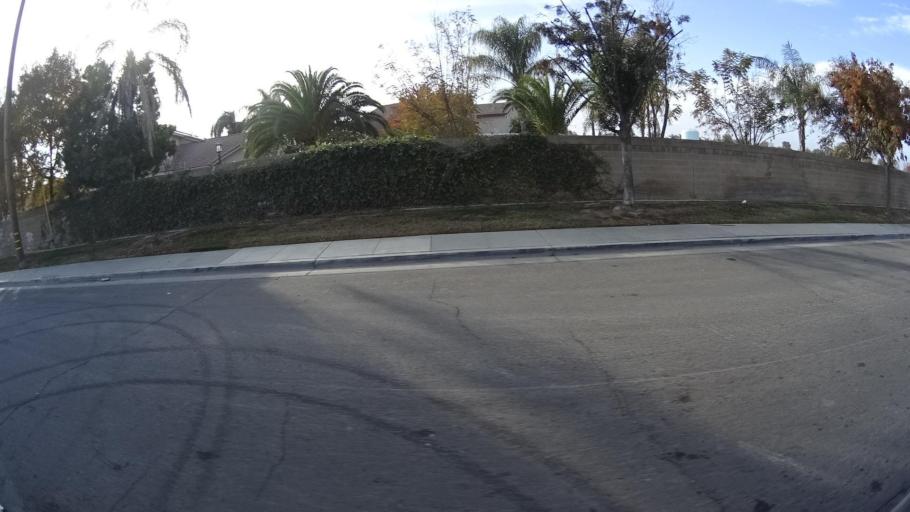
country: US
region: California
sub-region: Kern County
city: Delano
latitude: 35.7904
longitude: -119.2213
